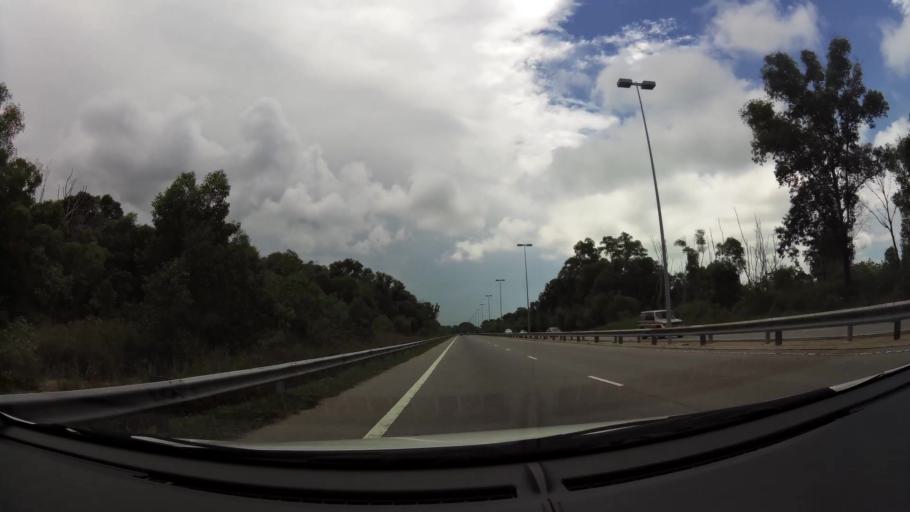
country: BN
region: Brunei and Muara
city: Bandar Seri Begawan
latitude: 4.9782
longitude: 114.8893
